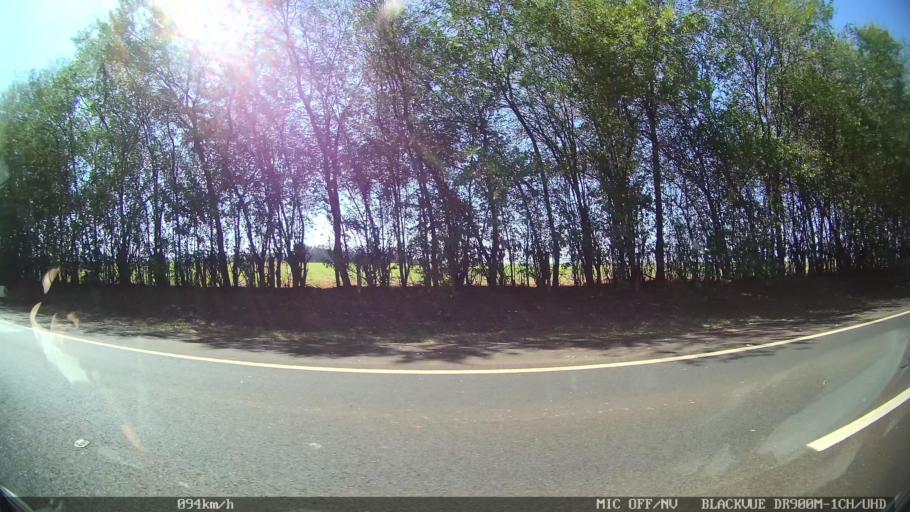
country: BR
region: Sao Paulo
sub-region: Batatais
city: Batatais
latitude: -20.7466
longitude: -47.5312
